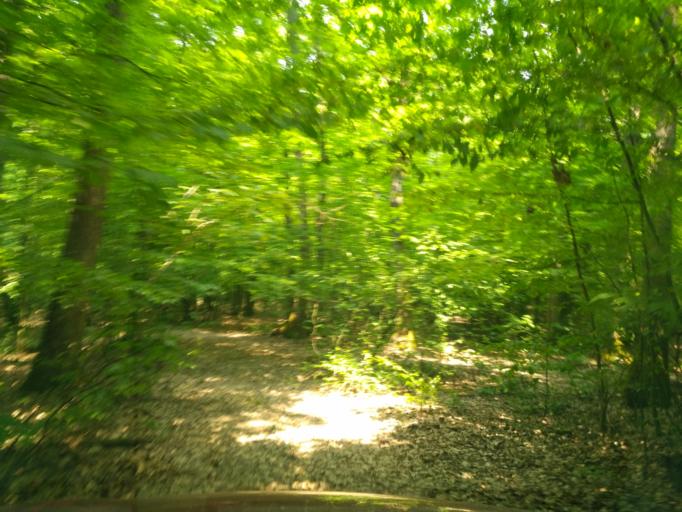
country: SK
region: Kosicky
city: Moldava nad Bodvou
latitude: 48.6494
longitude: 21.0351
